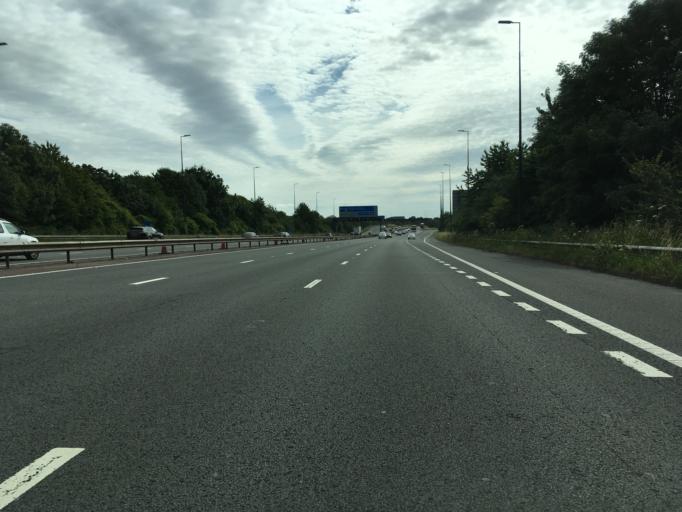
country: GB
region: Wales
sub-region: Monmouthshire
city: Magor
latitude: 51.5870
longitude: -2.8172
